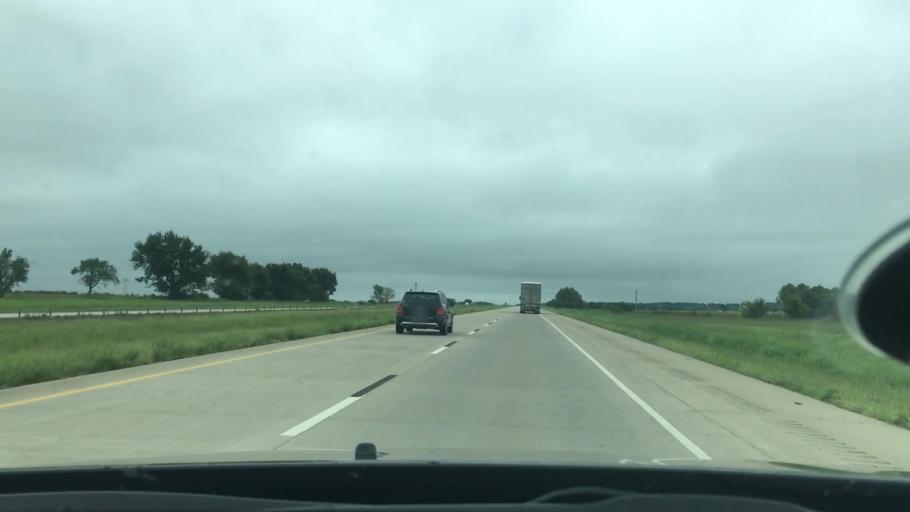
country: US
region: Oklahoma
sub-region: McIntosh County
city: Checotah
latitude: 35.4563
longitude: -95.4823
